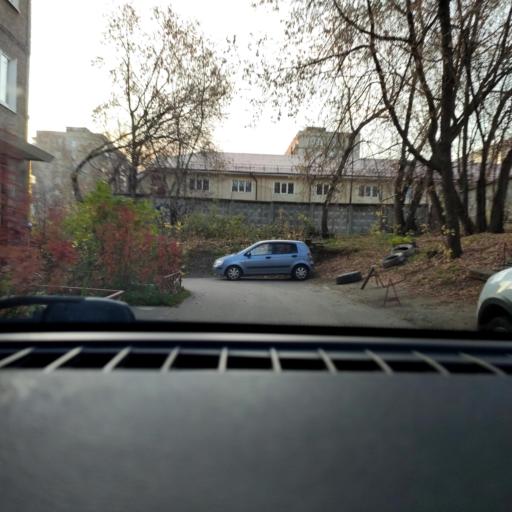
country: RU
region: Perm
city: Perm
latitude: 57.9944
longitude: 56.2308
